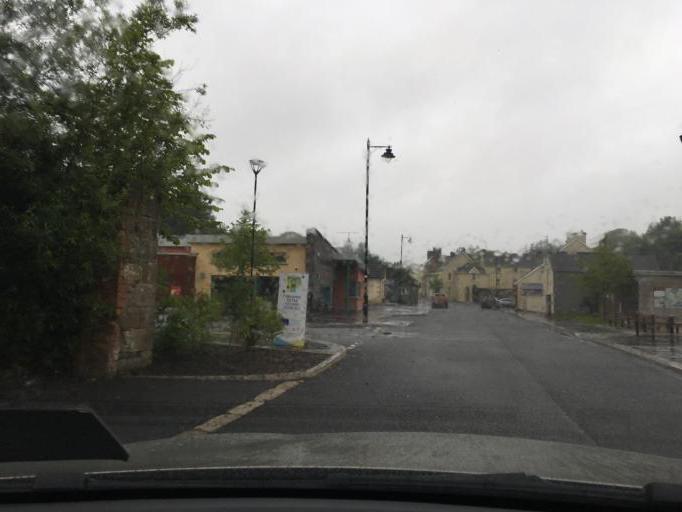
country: GB
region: Northern Ireland
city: Irvinestown
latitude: 54.5482
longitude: -7.8309
